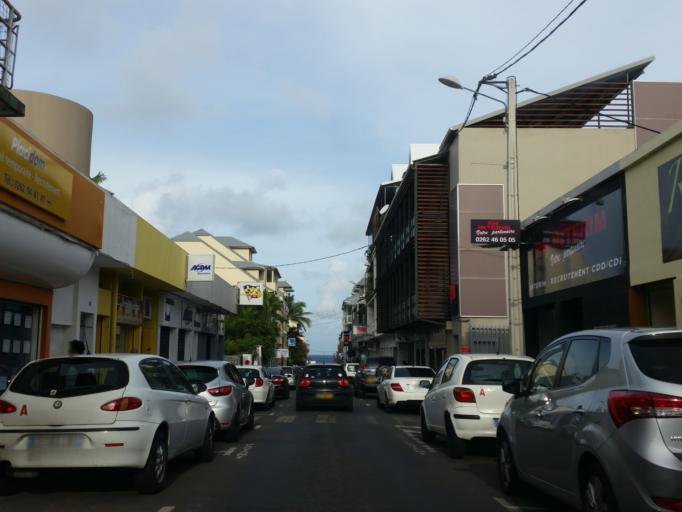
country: RE
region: Reunion
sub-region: Reunion
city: Saint-Denis
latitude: -20.8765
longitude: 55.4524
